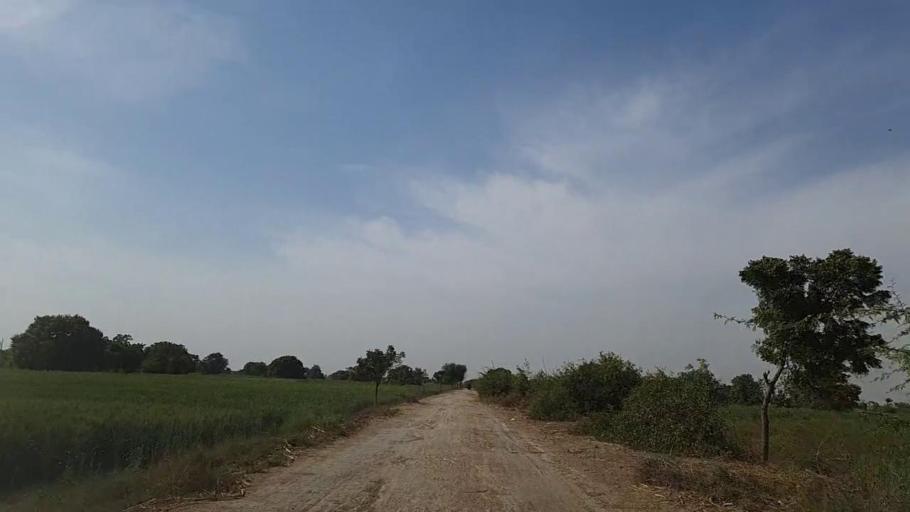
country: PK
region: Sindh
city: Samaro
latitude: 25.2321
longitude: 69.4281
